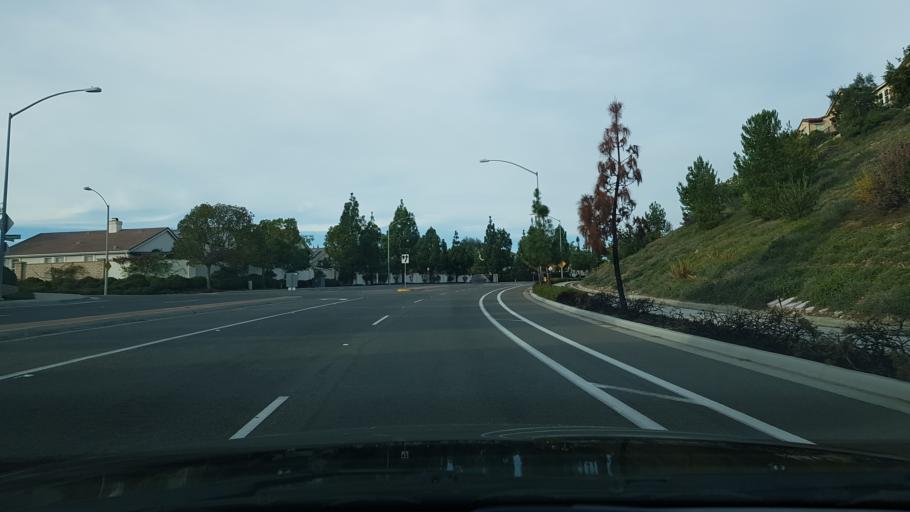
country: US
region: California
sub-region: San Diego County
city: Fairbanks Ranch
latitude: 32.9162
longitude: -117.1781
